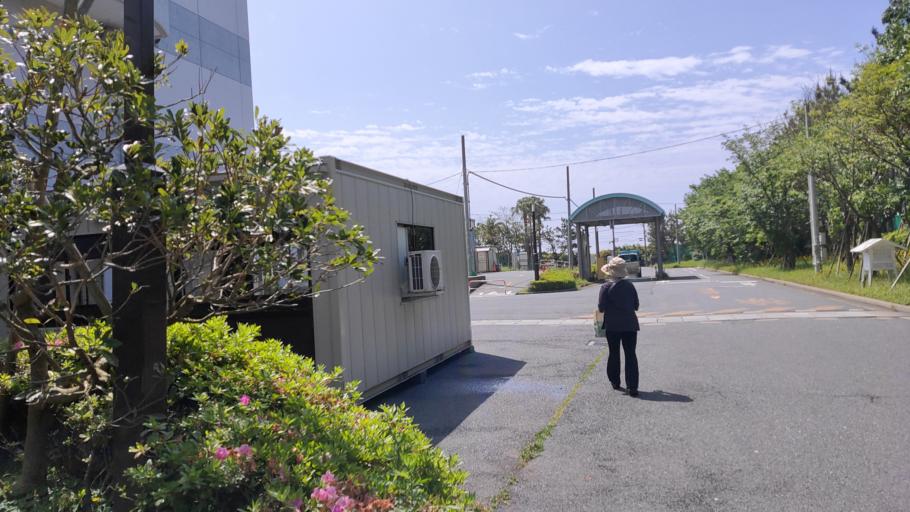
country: JP
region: Tokyo
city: Urayasu
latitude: 35.6188
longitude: 139.8981
